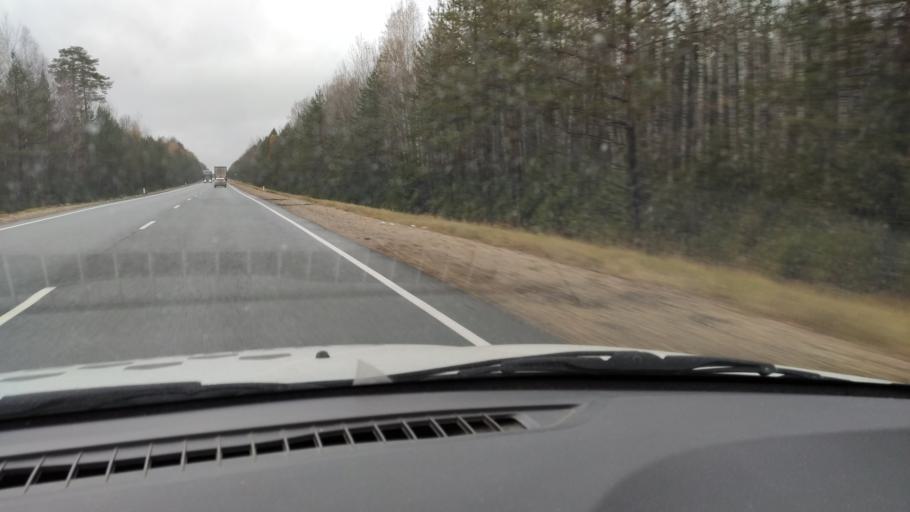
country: RU
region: Kirov
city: Chernaya Kholunitsa
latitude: 58.8590
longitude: 51.6673
